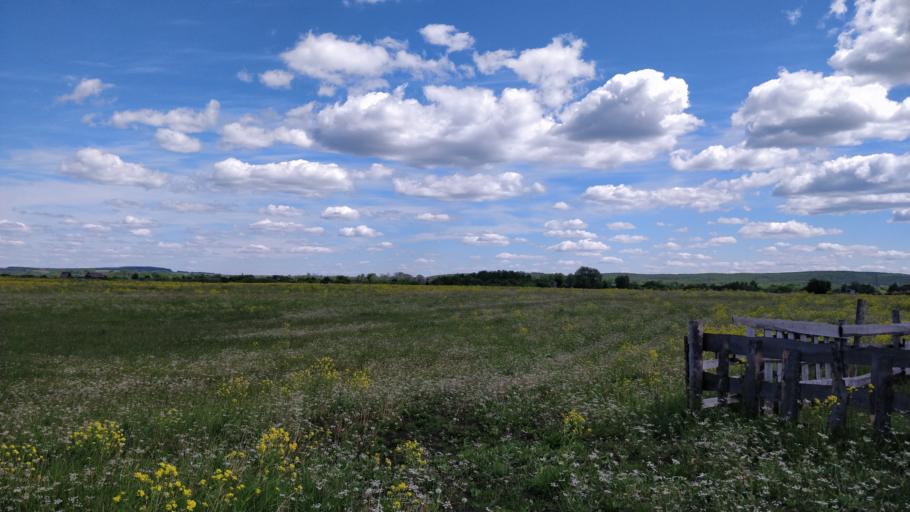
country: RU
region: Perm
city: Kungur
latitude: 57.4648
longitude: 56.9296
